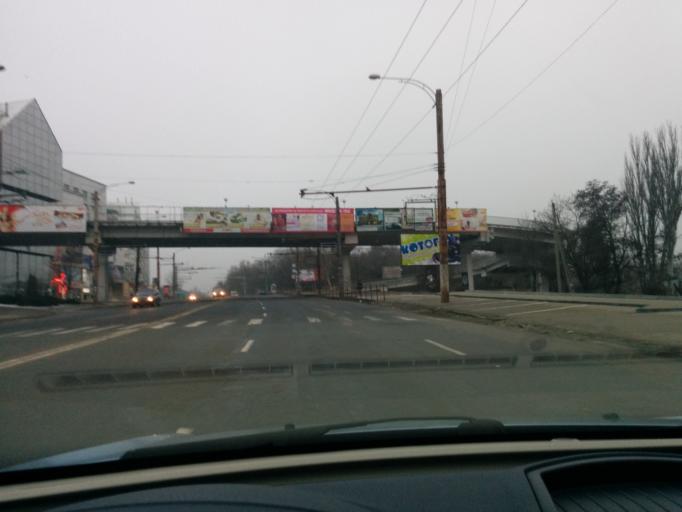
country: MD
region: Chisinau
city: Chisinau
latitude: 47.0059
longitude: 28.8587
